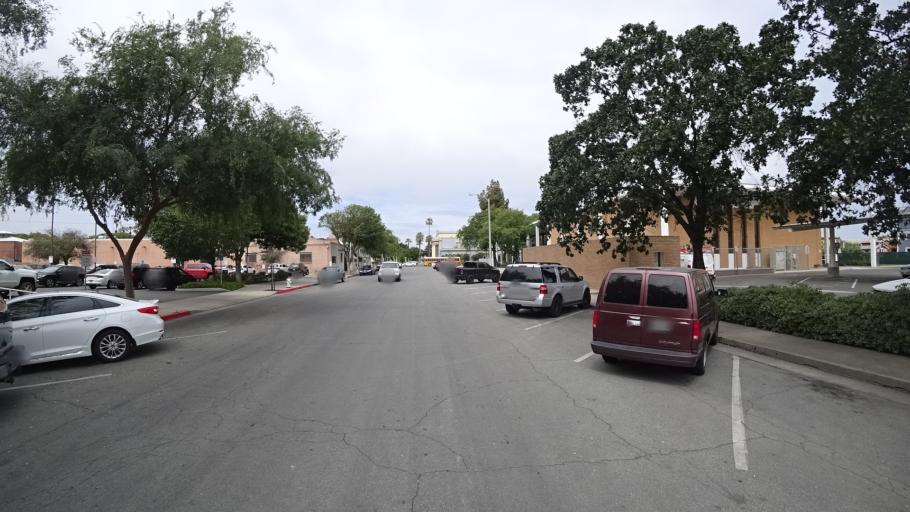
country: US
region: California
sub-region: Kings County
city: Hanford
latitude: 36.3290
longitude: -119.6448
